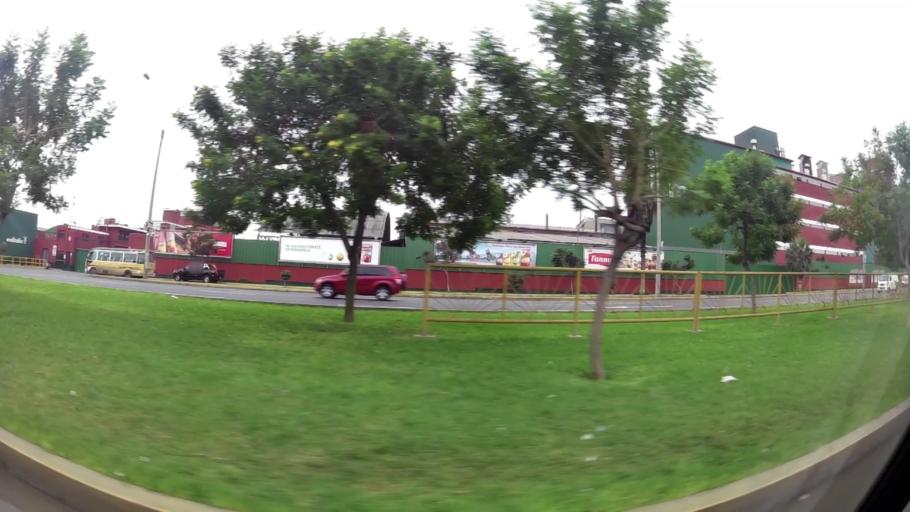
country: PE
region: Callao
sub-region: Callao
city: Callao
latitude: -12.0589
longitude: -77.0724
